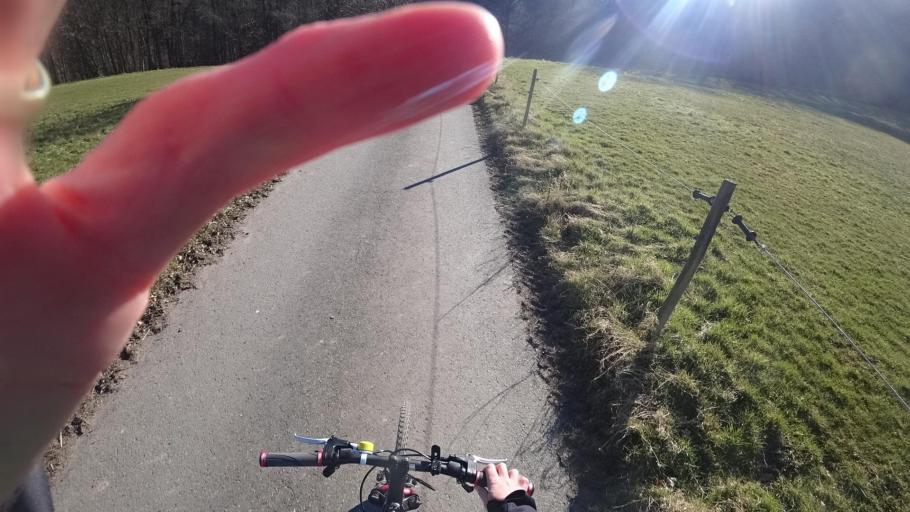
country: DE
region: Rheinland-Pfalz
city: Boppard
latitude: 50.2165
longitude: 7.5823
